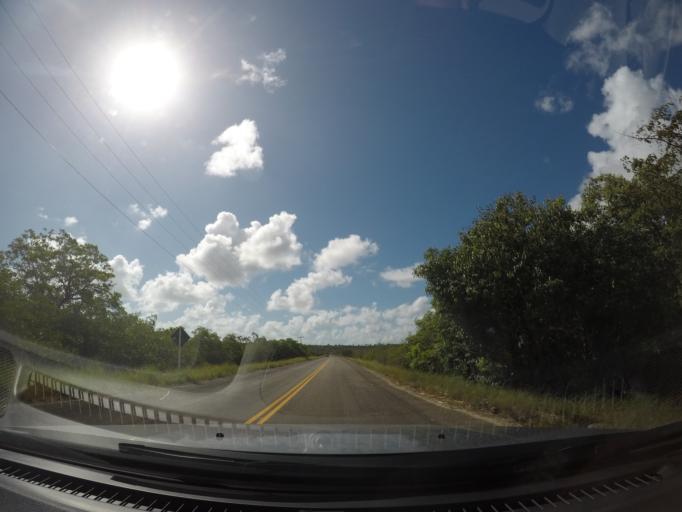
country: BR
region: Paraiba
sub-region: Pitimbu
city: Pitimbu
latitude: -7.4352
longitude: -34.8370
